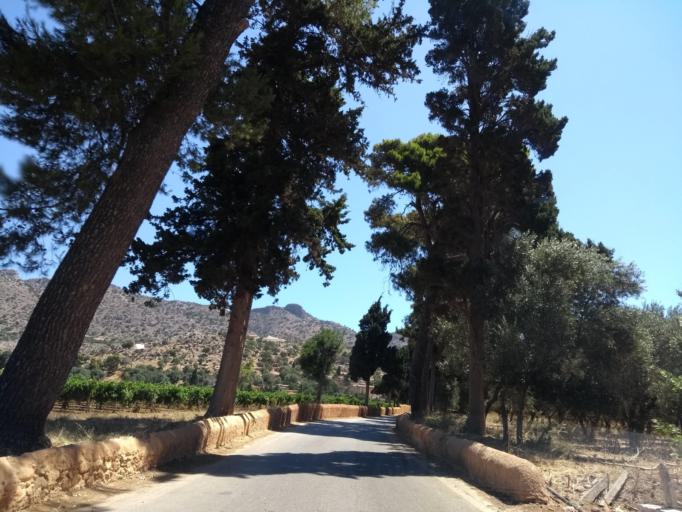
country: GR
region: Crete
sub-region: Nomos Chanias
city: Mouzouras
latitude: 35.5596
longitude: 24.1312
